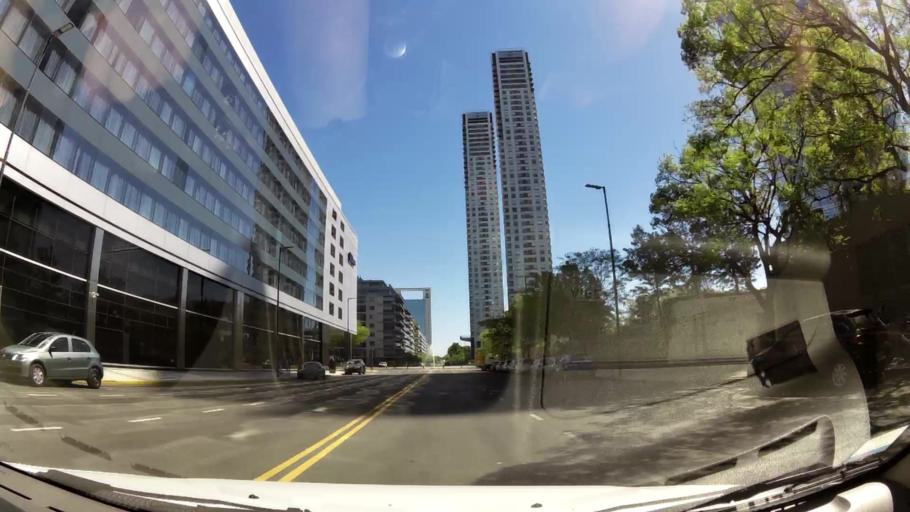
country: AR
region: Buenos Aires F.D.
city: Buenos Aires
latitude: -34.6061
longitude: -58.3633
